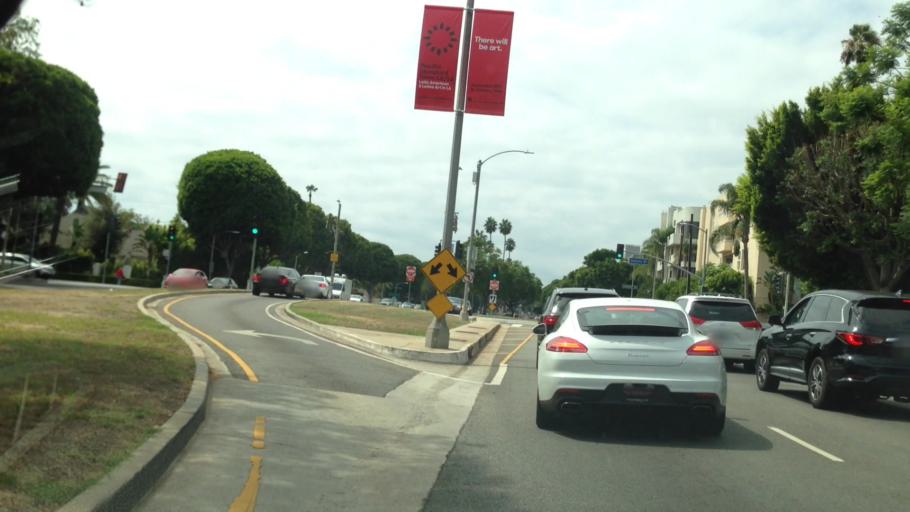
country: US
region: California
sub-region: Los Angeles County
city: Beverly Hills
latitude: 34.0723
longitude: -118.3890
